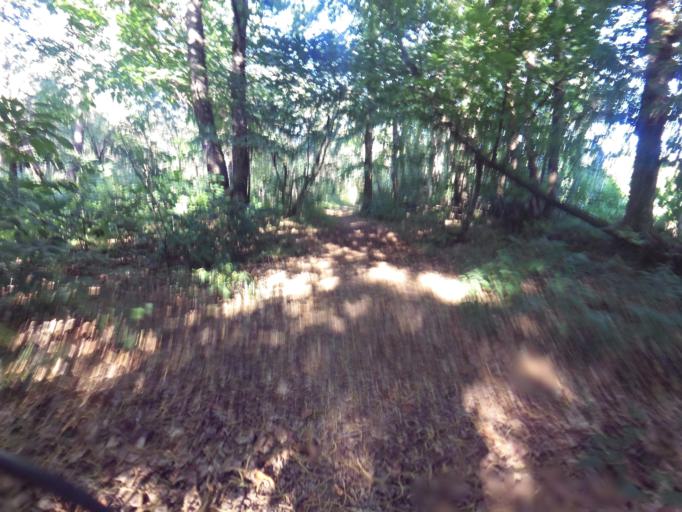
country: FR
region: Brittany
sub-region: Departement du Morbihan
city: Molac
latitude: 47.7537
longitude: -2.4134
